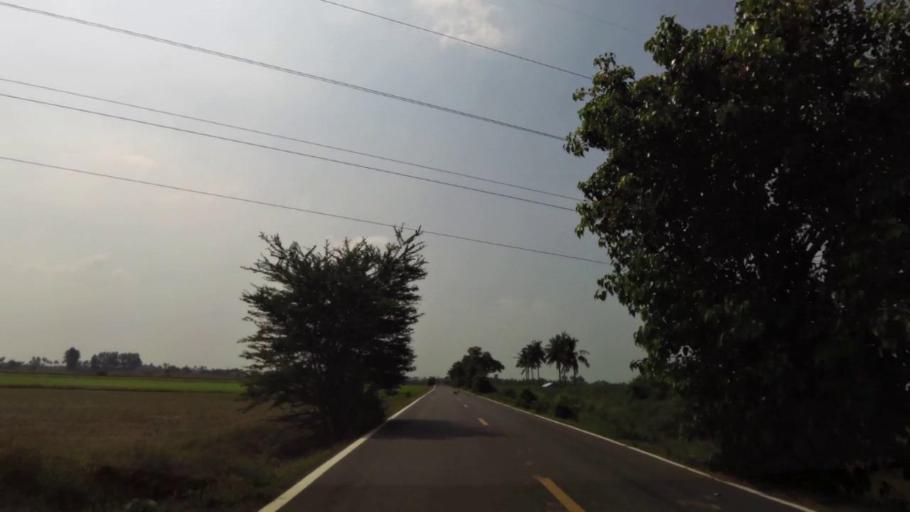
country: TH
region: Ang Thong
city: Pho Thong
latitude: 14.6177
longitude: 100.4016
